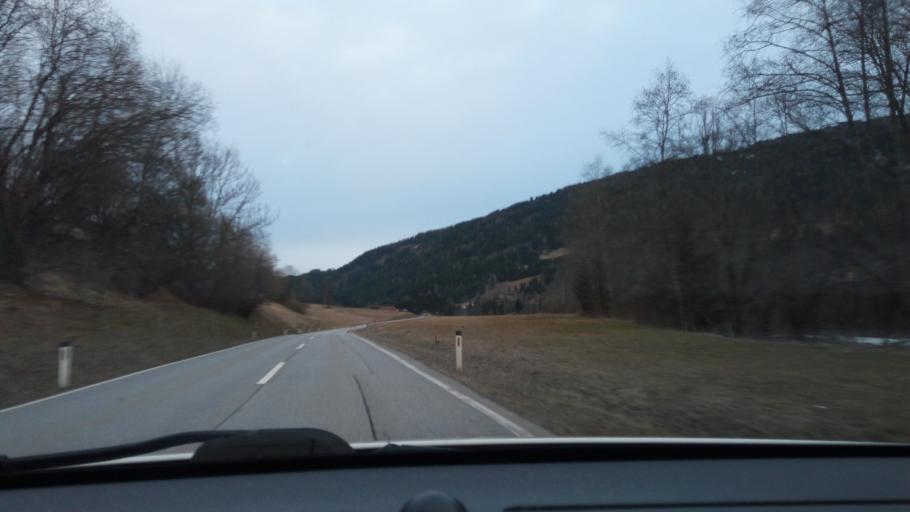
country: AT
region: Styria
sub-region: Politischer Bezirk Murau
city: Sankt Georgen ob Murau
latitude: 47.1060
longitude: 14.1154
